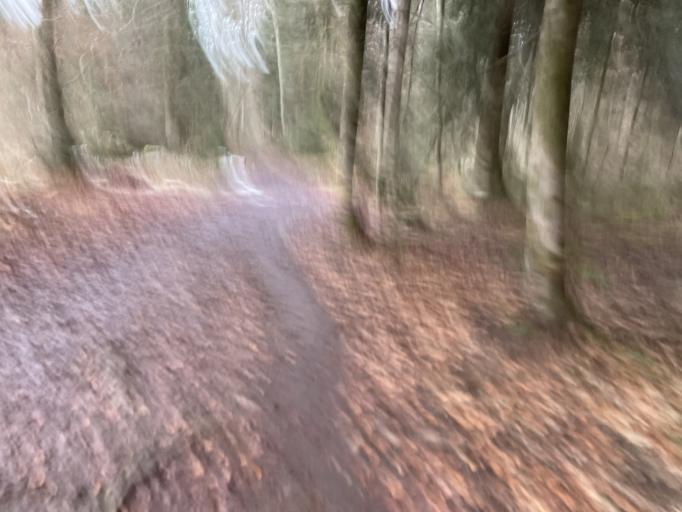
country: CH
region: Bern
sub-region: Thun District
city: Uttigen
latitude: 46.8083
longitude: 7.5692
